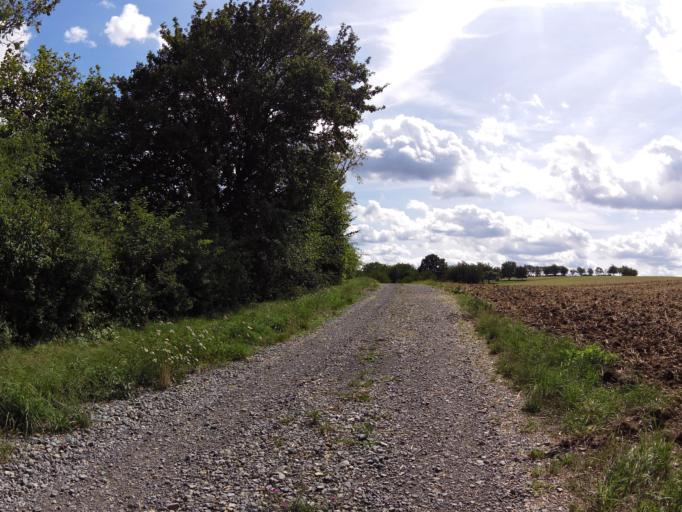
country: DE
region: Bavaria
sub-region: Regierungsbezirk Unterfranken
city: Margetshochheim
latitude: 49.8411
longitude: 9.8475
